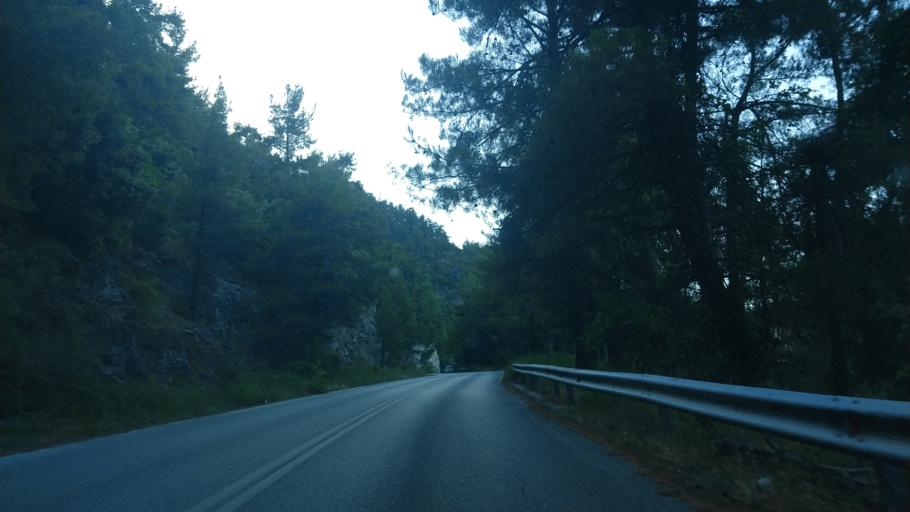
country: GR
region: East Macedonia and Thrace
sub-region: Nomos Kavalas
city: Potamia
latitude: 40.7225
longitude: 24.7338
